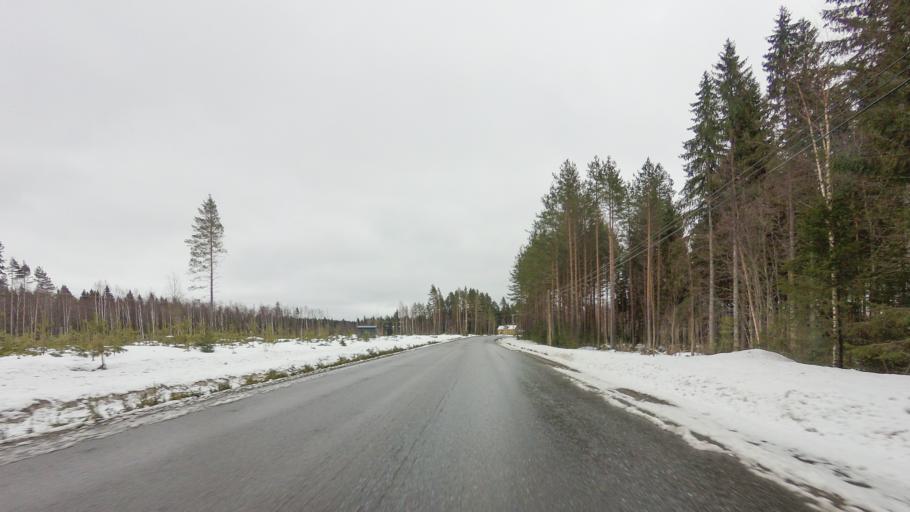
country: FI
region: Southern Savonia
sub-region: Savonlinna
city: Savonlinna
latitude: 61.9280
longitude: 28.8883
